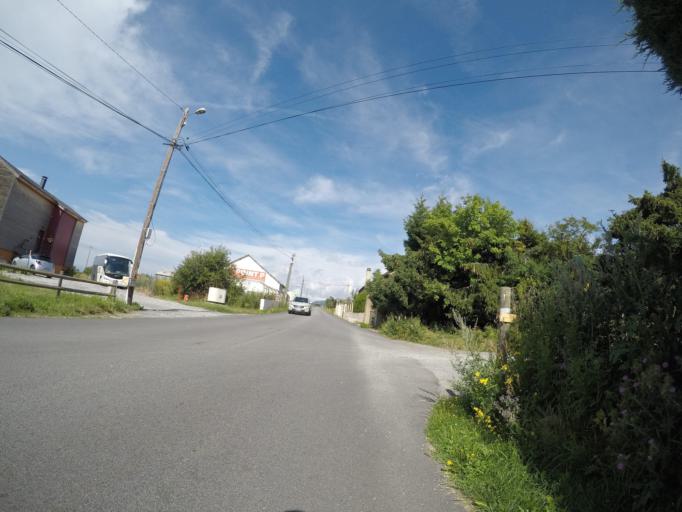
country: ES
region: Catalonia
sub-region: Provincia de Girona
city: Llivia
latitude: 42.4982
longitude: 2.0904
